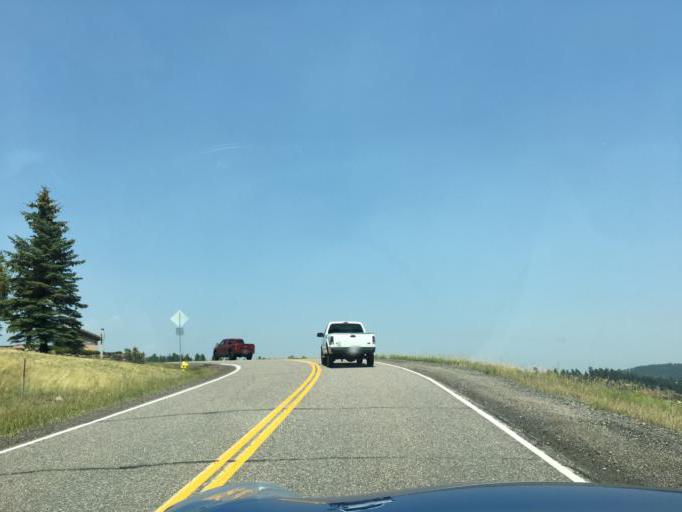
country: US
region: Colorado
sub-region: Jefferson County
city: Genesee
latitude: 39.7041
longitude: -105.2805
